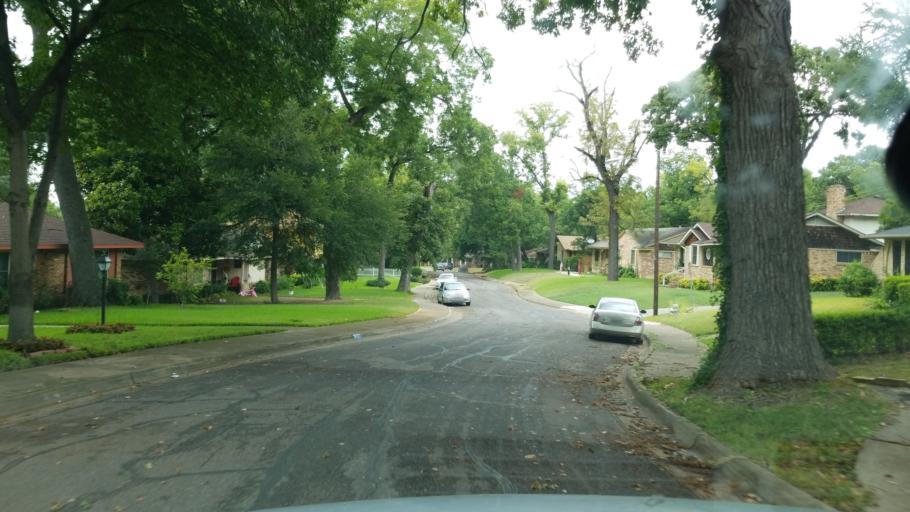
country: US
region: Texas
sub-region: Dallas County
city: Duncanville
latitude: 32.6703
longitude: -96.8361
